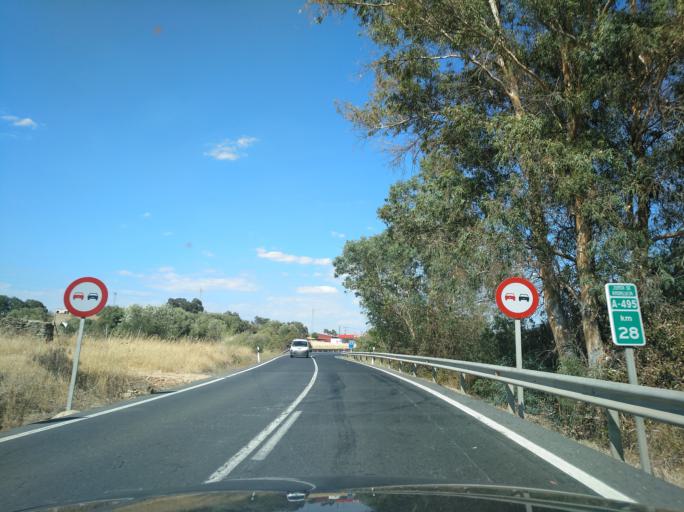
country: ES
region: Andalusia
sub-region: Provincia de Huelva
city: Alosno
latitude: 37.5444
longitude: -7.1256
